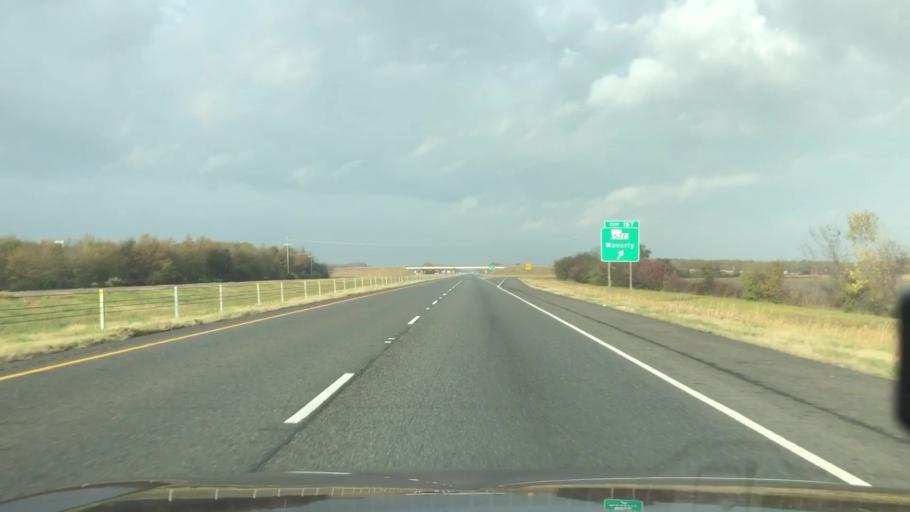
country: US
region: Louisiana
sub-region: Richland Parish
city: Delhi
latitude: 32.4306
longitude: -91.4118
